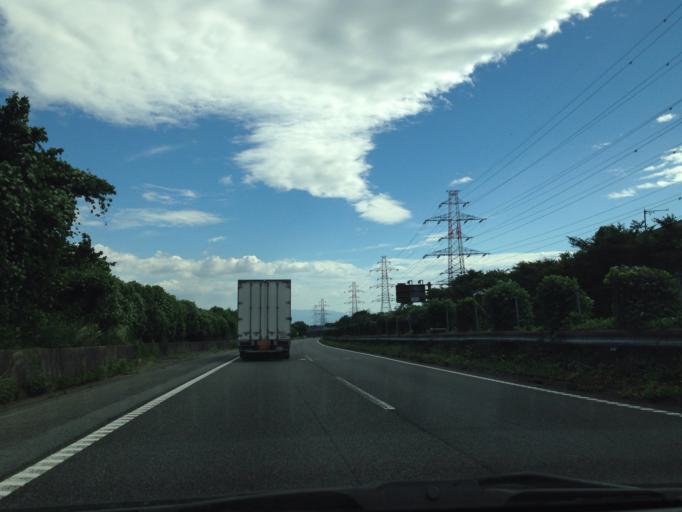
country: JP
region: Shizuoka
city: Gotemba
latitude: 35.2475
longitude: 138.9101
